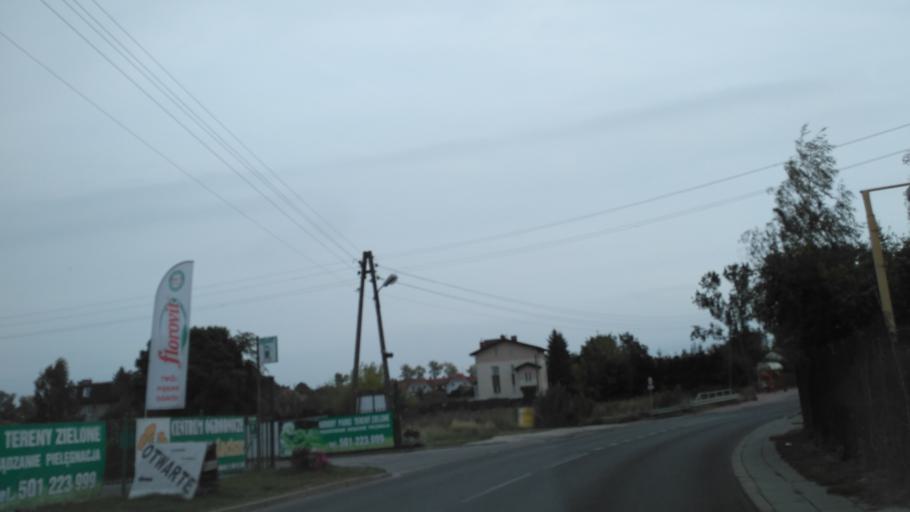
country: PL
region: Lublin Voivodeship
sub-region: Powiat lubelski
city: Lublin
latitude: 51.2079
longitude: 22.5982
